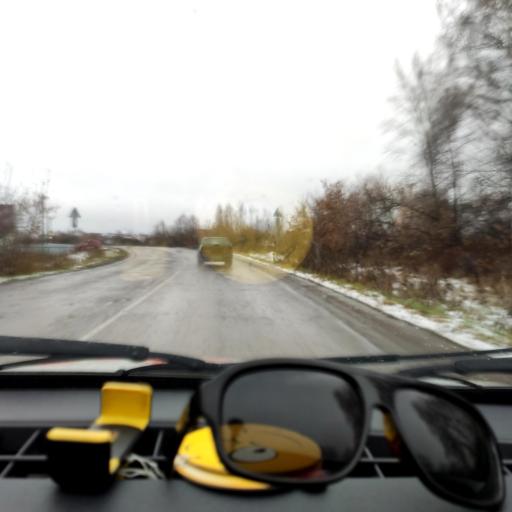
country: RU
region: Bashkortostan
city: Iglino
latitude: 54.8788
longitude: 56.5512
